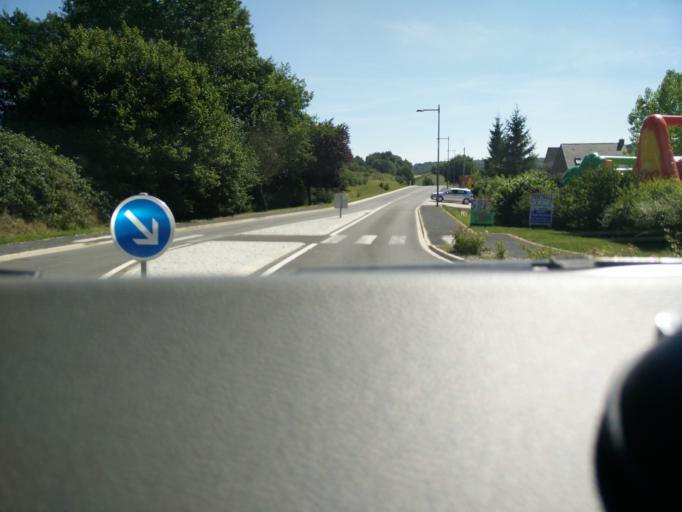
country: FR
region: Nord-Pas-de-Calais
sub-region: Departement du Nord
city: Trelon
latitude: 50.1211
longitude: 4.0998
